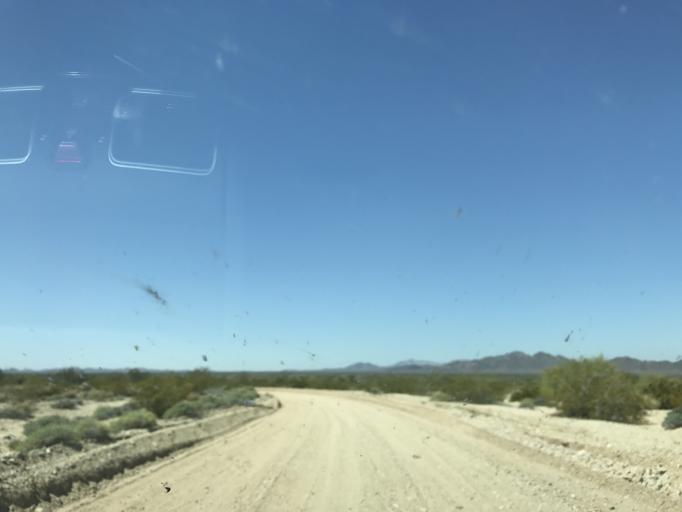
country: US
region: California
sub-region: Riverside County
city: Mesa Verde
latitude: 33.4942
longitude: -114.8803
